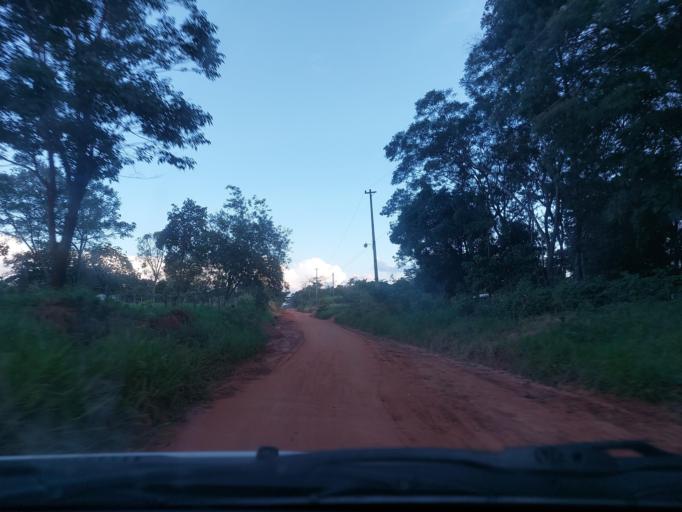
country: PY
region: San Pedro
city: Lima
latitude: -24.1451
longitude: -56.0113
